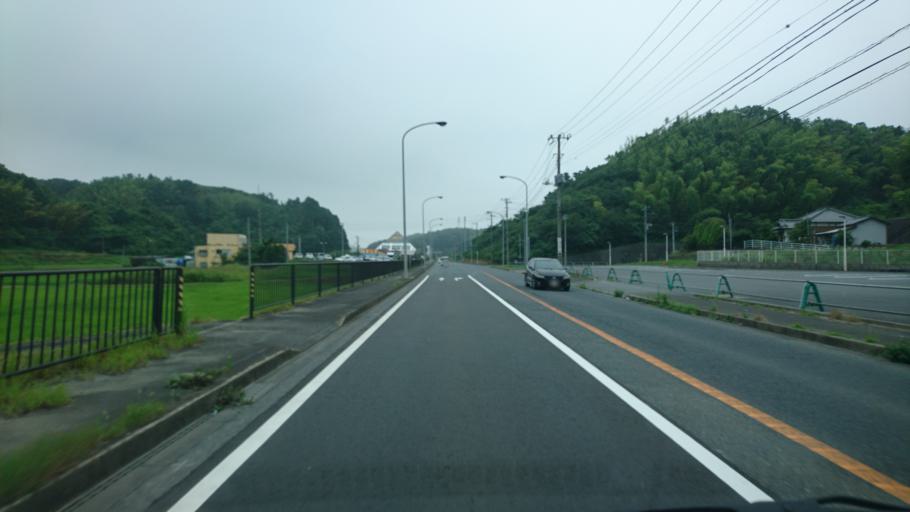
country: JP
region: Chiba
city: Kimitsu
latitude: 35.2737
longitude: 139.9018
